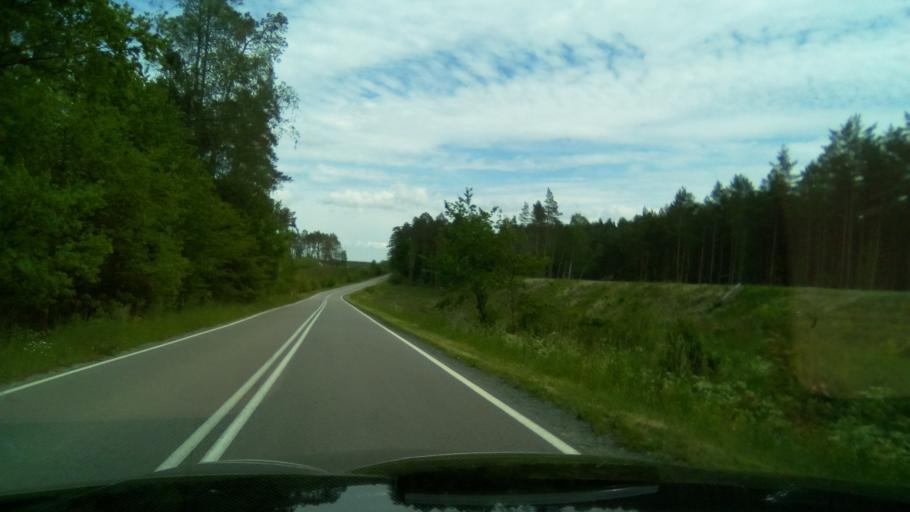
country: PL
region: Pomeranian Voivodeship
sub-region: Powiat bytowski
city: Czarna Dabrowka
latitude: 54.3655
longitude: 17.6018
